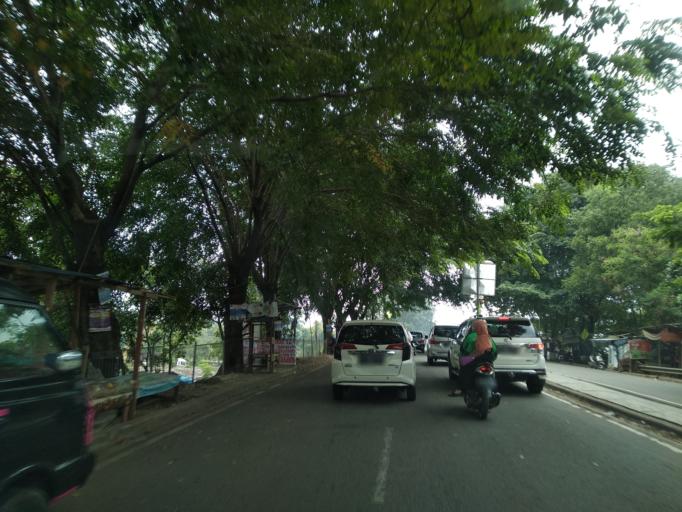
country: ID
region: West Java
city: Bekasi
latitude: -6.2740
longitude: 107.0453
